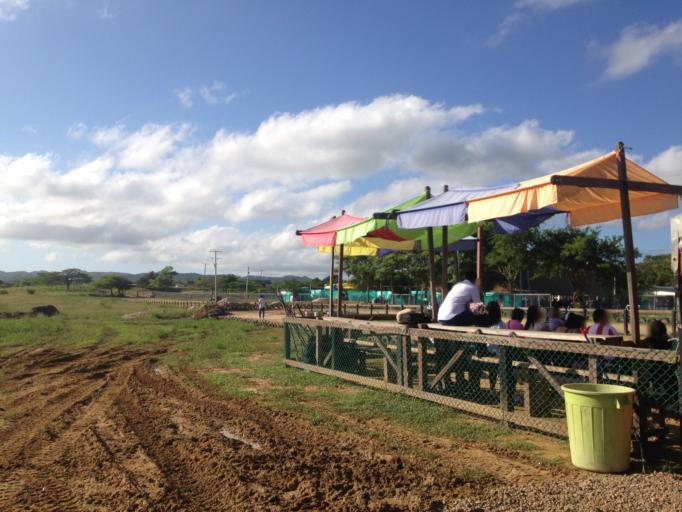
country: CO
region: Atlantico
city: Baranoa
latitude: 10.8403
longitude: -74.9027
